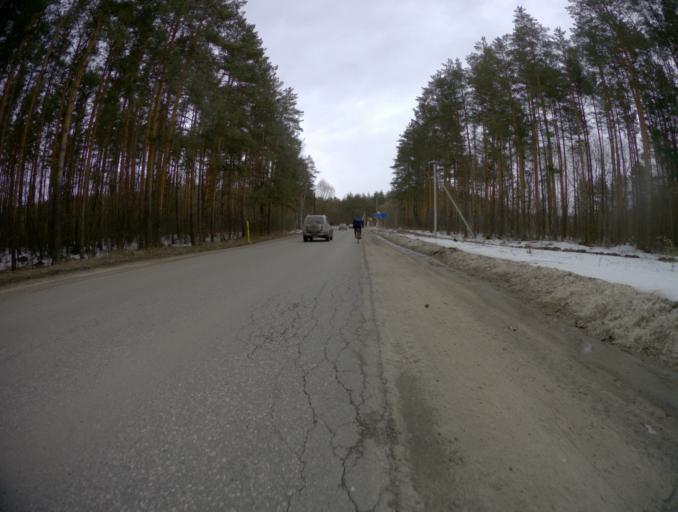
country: RU
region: Vladimir
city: Kommunar
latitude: 56.1312
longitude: 40.4879
